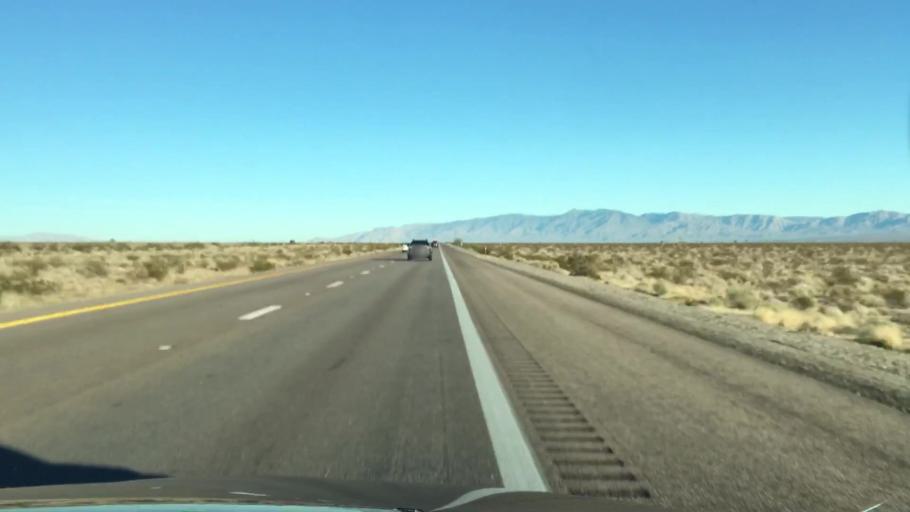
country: US
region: Nevada
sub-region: Clark County
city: Bunkerville
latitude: 36.7667
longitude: -114.3300
